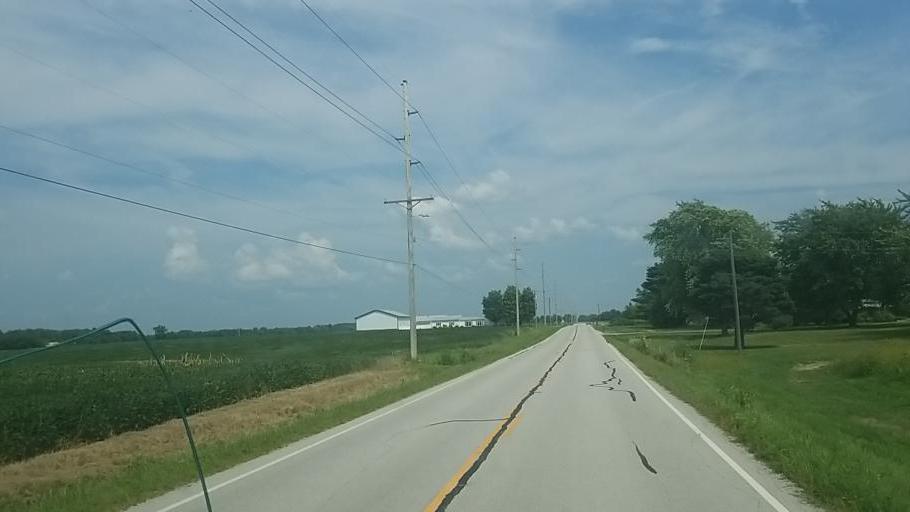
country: US
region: Ohio
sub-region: Hardin County
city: Forest
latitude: 40.7819
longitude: -83.5484
